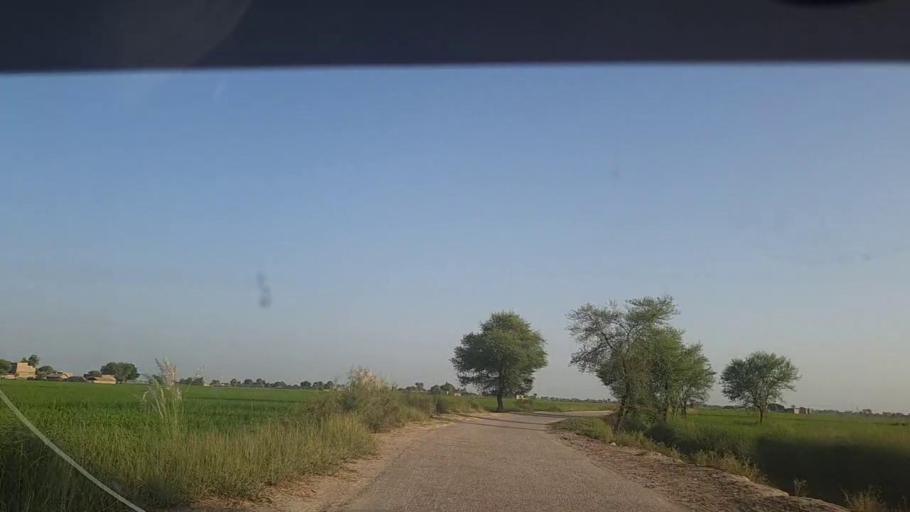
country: PK
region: Sindh
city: Thul
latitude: 28.2014
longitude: 68.8740
